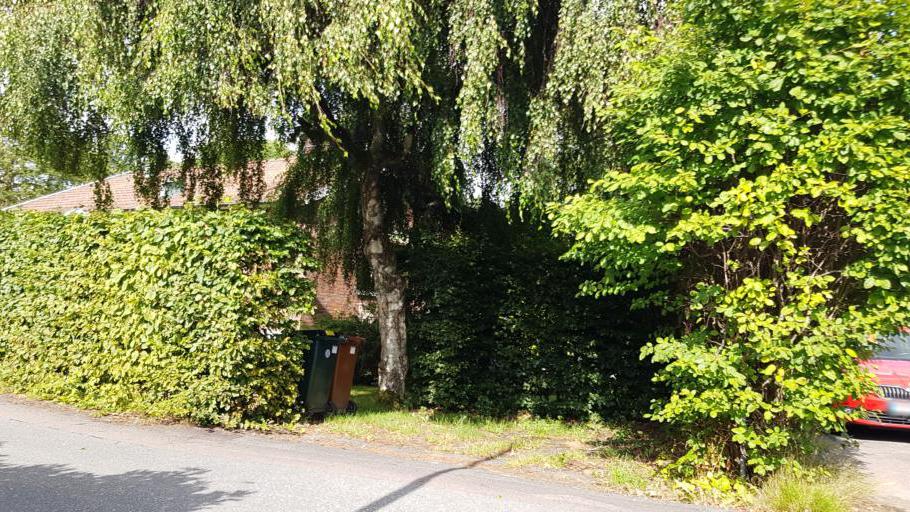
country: SE
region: Vaestra Goetaland
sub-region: Harryda Kommun
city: Molnlycke
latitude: 57.6595
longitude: 12.1105
